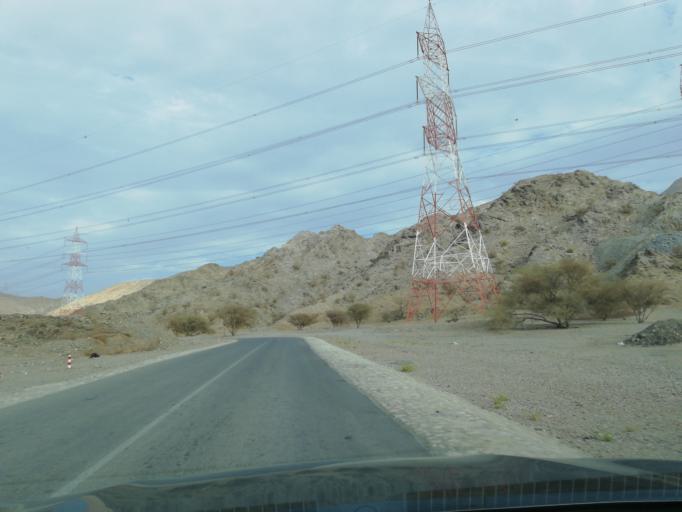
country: OM
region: Muhafazat Masqat
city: Bawshar
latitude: 23.4706
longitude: 58.3125
